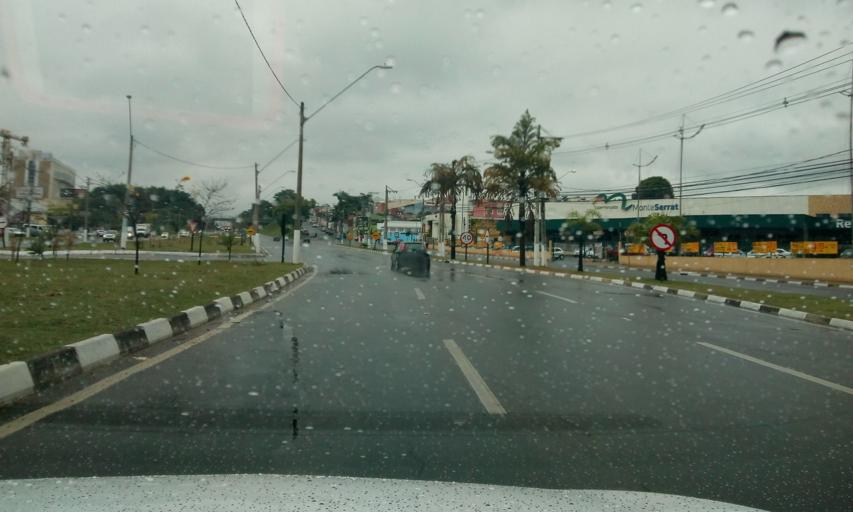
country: BR
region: Sao Paulo
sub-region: Itupeva
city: Itupeva
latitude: -23.1572
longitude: -47.0414
